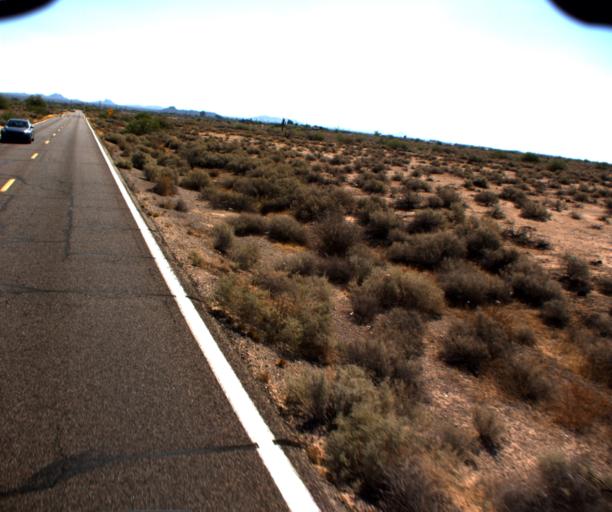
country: US
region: Arizona
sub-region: Pinal County
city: Sacaton
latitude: 33.0581
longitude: -111.6942
